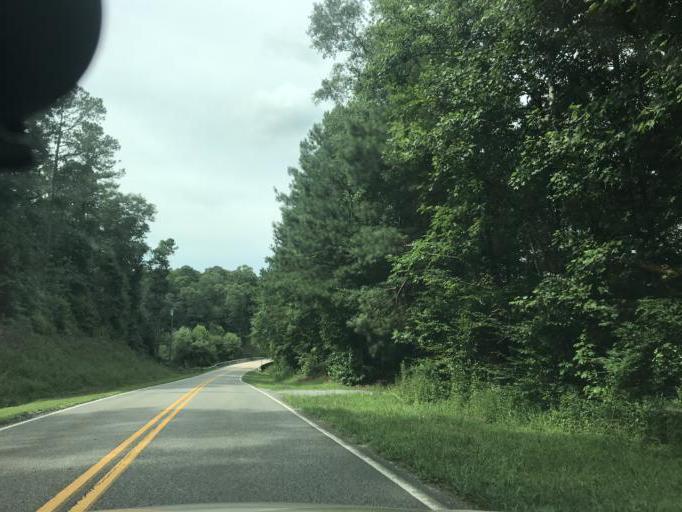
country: US
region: Georgia
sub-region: Forsyth County
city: Cumming
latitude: 34.2898
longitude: -84.2417
